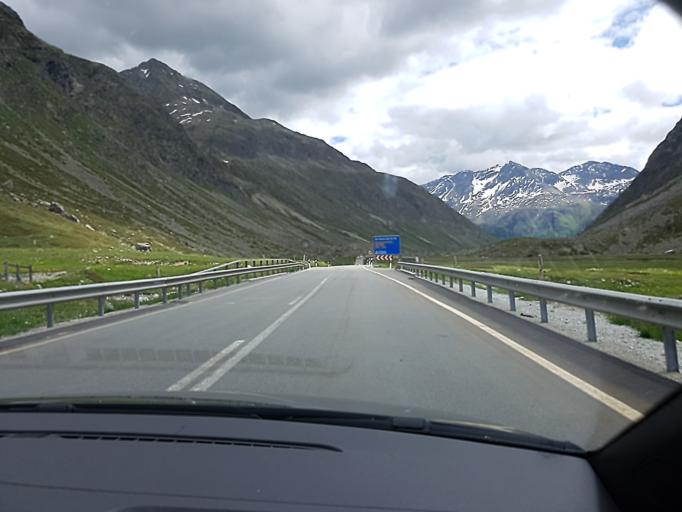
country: CH
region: Grisons
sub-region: Maloja District
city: Silvaplana
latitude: 46.4725
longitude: 9.7402
